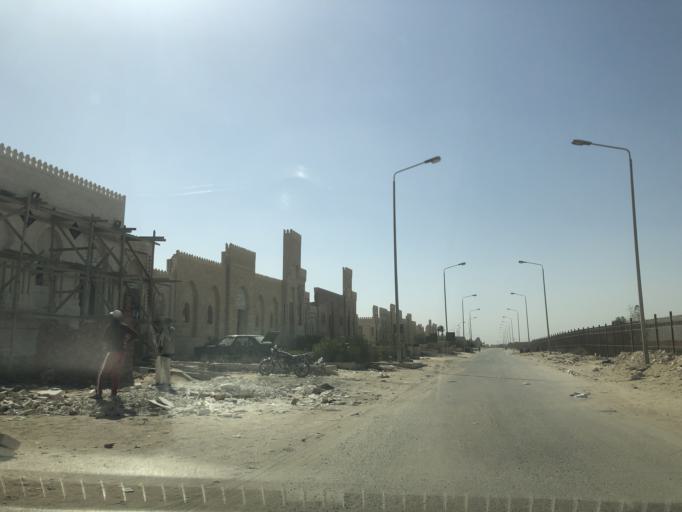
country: EG
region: Al Jizah
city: Madinat Sittah Uktubar
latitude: 29.9264
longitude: 30.9525
